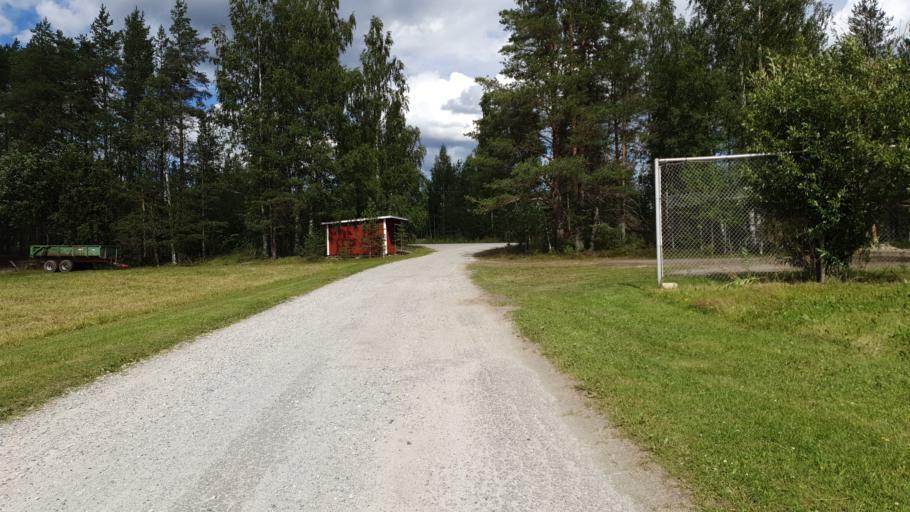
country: FI
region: Kainuu
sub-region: Kehys-Kainuu
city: Kuhmo
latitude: 64.3817
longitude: 29.7816
